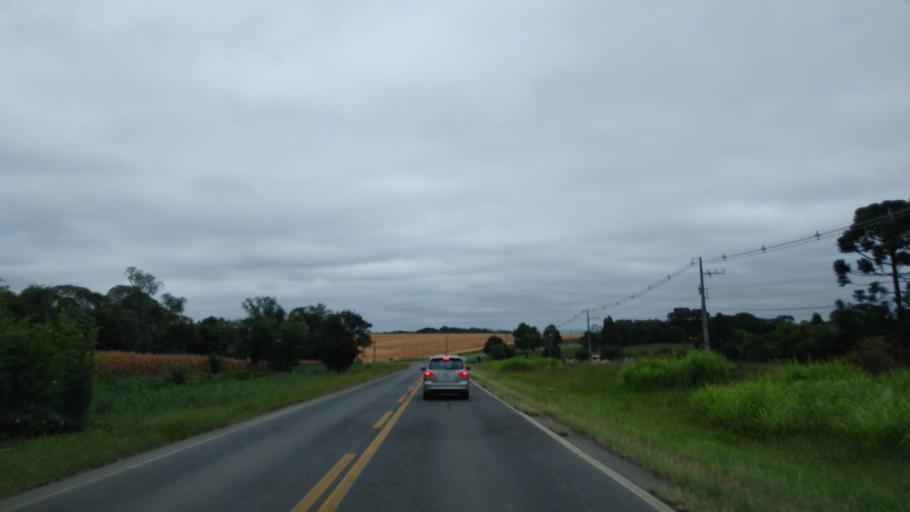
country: BR
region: Santa Catarina
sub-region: Canoinhas
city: Canoinhas
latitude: -26.2298
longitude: -50.4638
